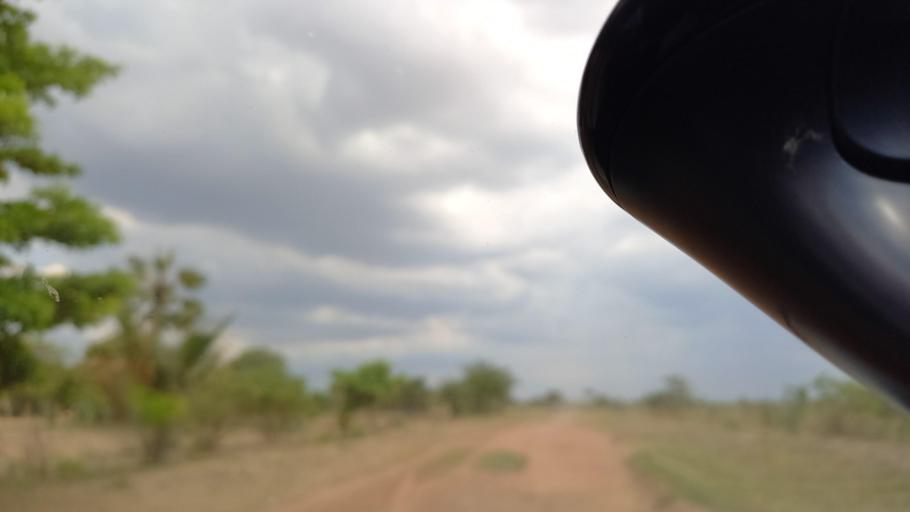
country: ZM
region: Lusaka
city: Kafue
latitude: -15.8341
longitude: 28.0718
